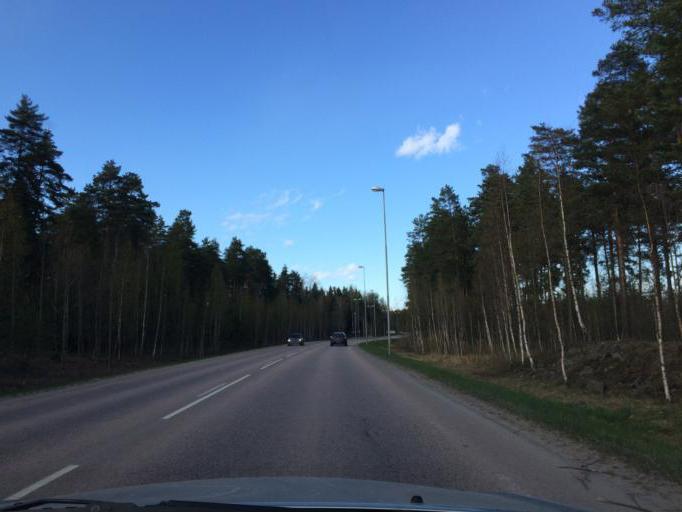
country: SE
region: Vaestmanland
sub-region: Vasteras
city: Vasteras
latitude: 59.6407
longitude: 16.5510
